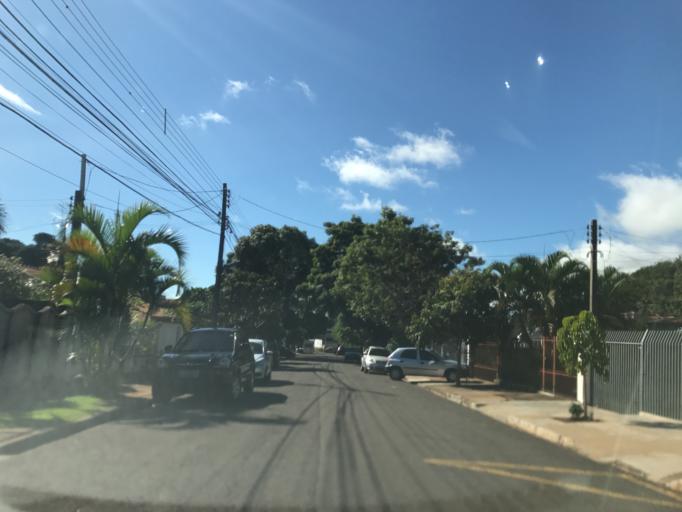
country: BR
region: Parana
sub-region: Maringa
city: Maringa
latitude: -23.4519
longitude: -51.9560
